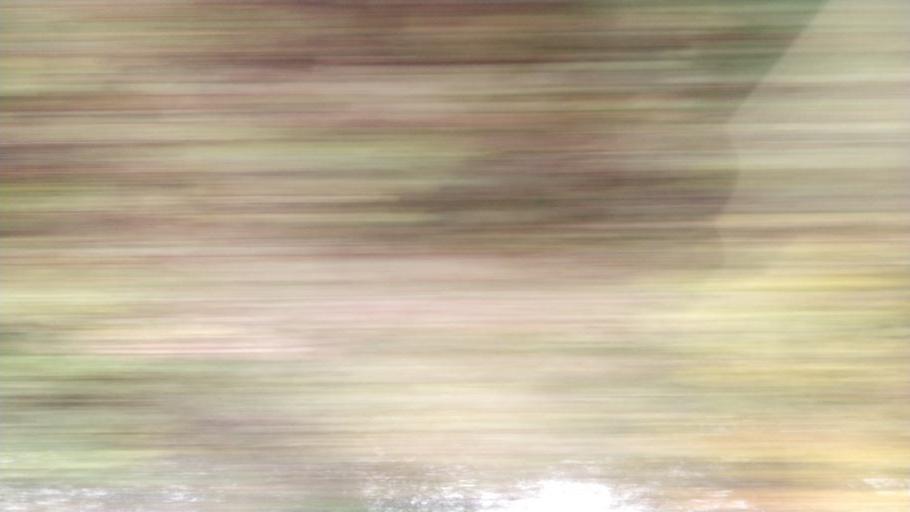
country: GB
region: England
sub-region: Borough of Wigan
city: Shevington
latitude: 53.5559
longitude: -2.6688
